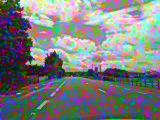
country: IE
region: Ulster
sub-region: County Donegal
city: Letterkenny
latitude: 54.8716
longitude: -7.7474
